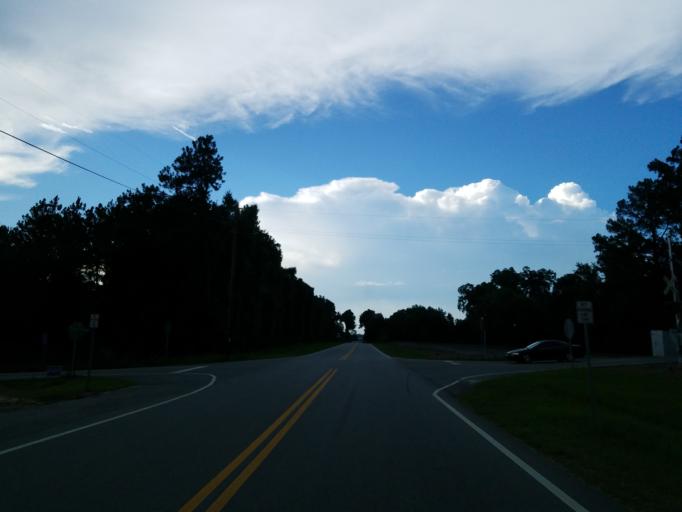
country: US
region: Georgia
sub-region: Tift County
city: Unionville
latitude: 31.3588
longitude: -83.4859
